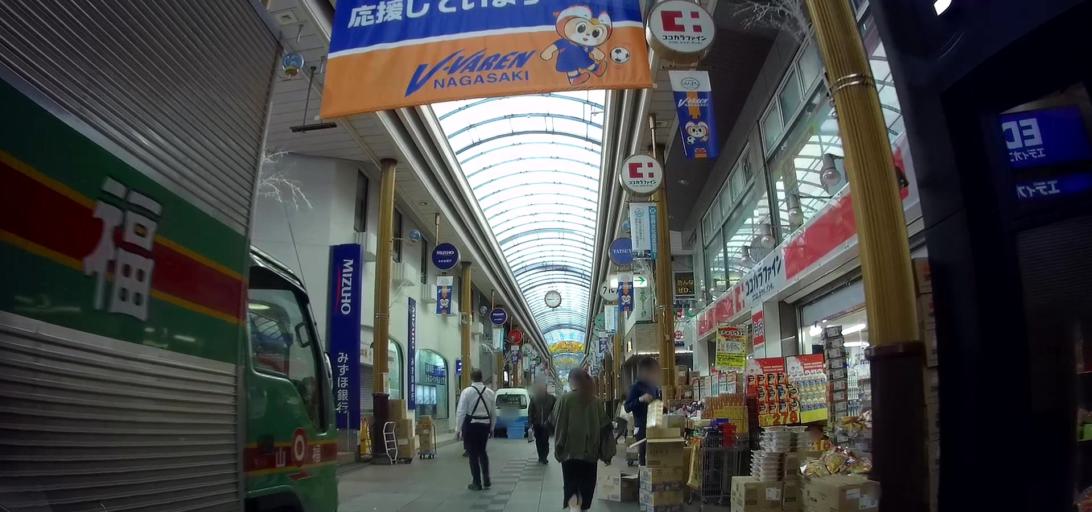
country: JP
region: Nagasaki
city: Nagasaki-shi
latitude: 32.7445
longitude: 129.8772
